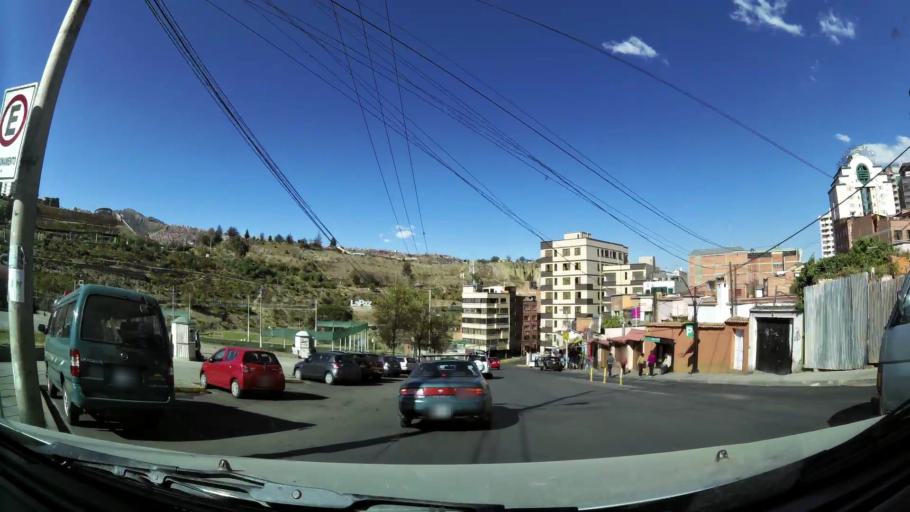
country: BO
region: La Paz
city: La Paz
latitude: -16.5044
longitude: -68.1278
